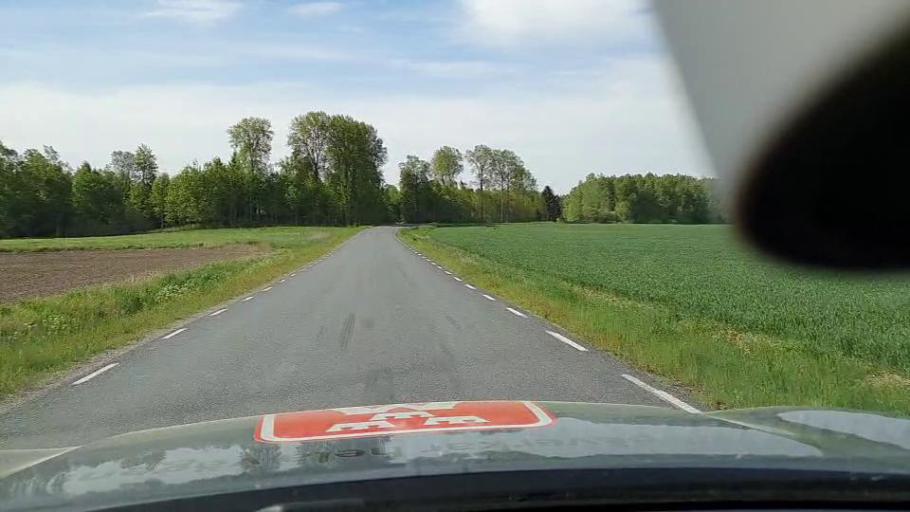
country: SE
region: Soedermanland
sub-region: Eskilstuna Kommun
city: Arla
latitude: 59.2687
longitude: 16.6606
